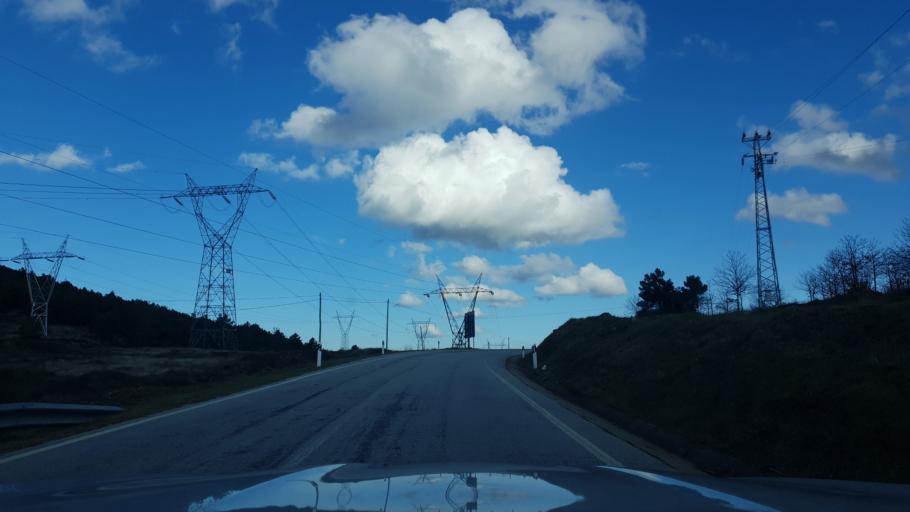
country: PT
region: Braganca
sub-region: Torre de Moncorvo
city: Torre de Moncorvo
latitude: 41.1886
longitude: -6.9572
